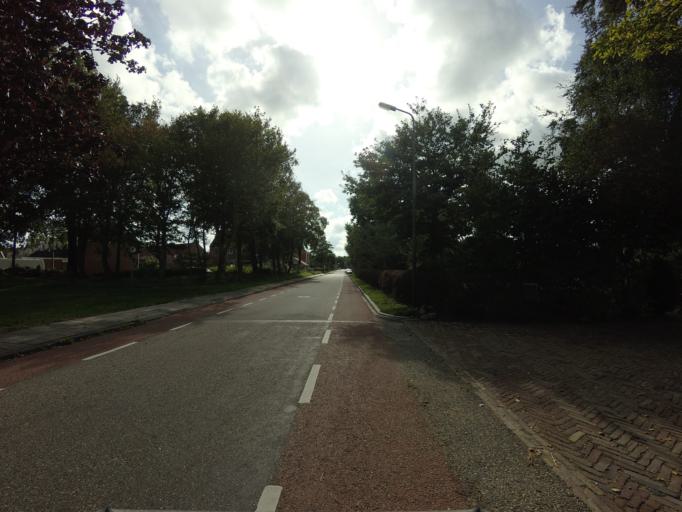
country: NL
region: North Holland
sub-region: Gemeente Hollands Kroon
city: Den Oever
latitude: 52.9148
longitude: 4.9668
